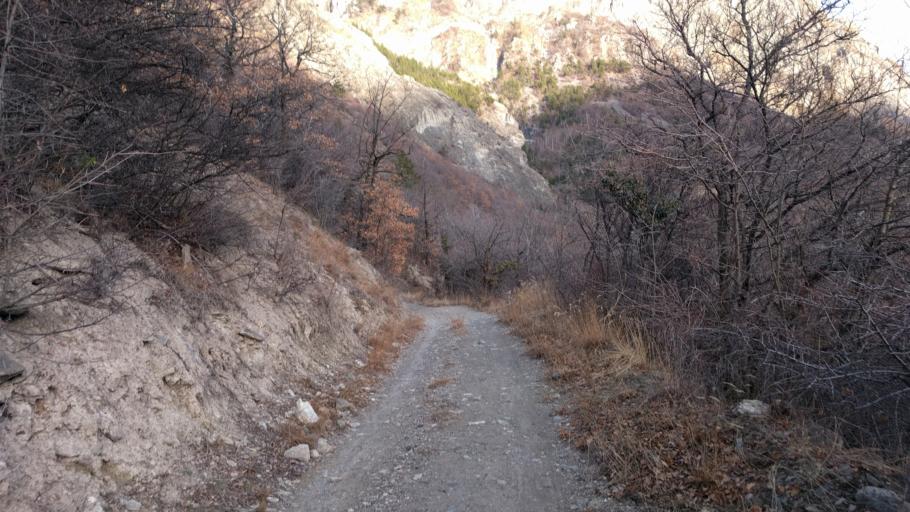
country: FR
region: Rhone-Alpes
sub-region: Departement de la Savoie
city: Villargondran
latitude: 45.2569
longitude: 6.4197
